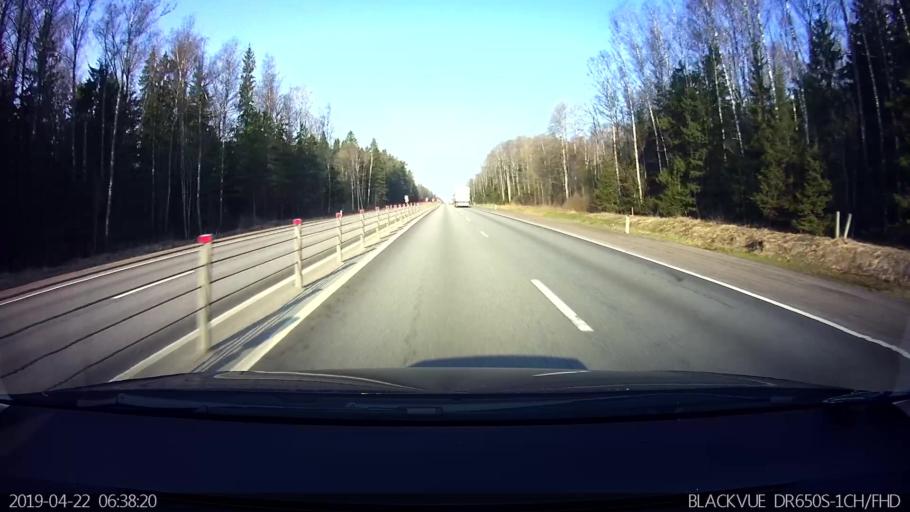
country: RU
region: Moskovskaya
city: Uvarovka
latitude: 55.4914
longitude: 35.3769
